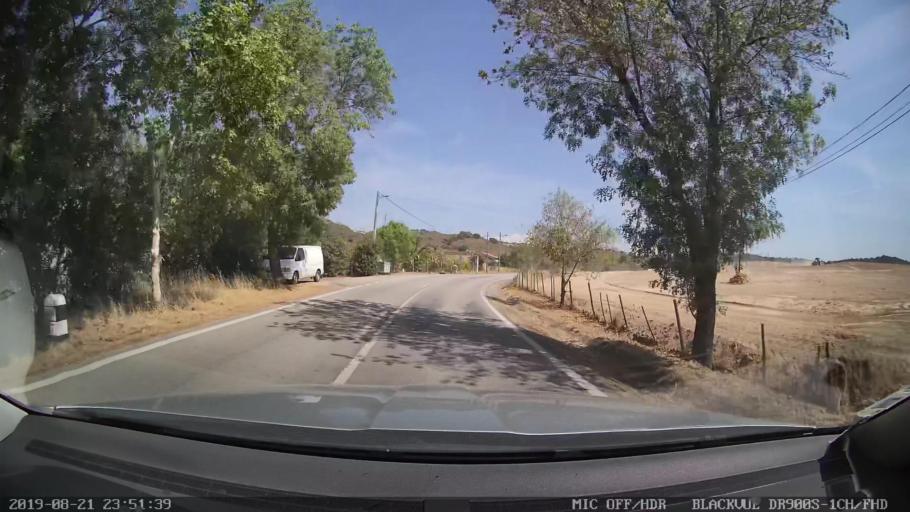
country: PT
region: Castelo Branco
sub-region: Idanha-A-Nova
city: Idanha-a-Nova
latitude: 39.9046
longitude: -7.2339
